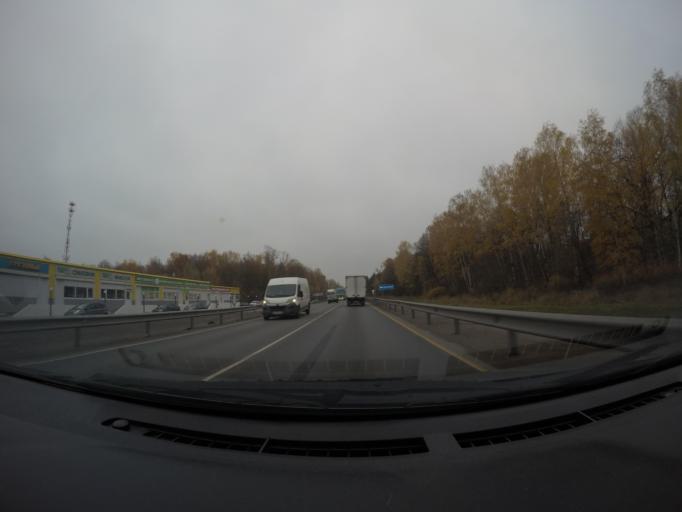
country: RU
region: Moskovskaya
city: Bronnitsy
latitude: 55.4052
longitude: 38.2292
